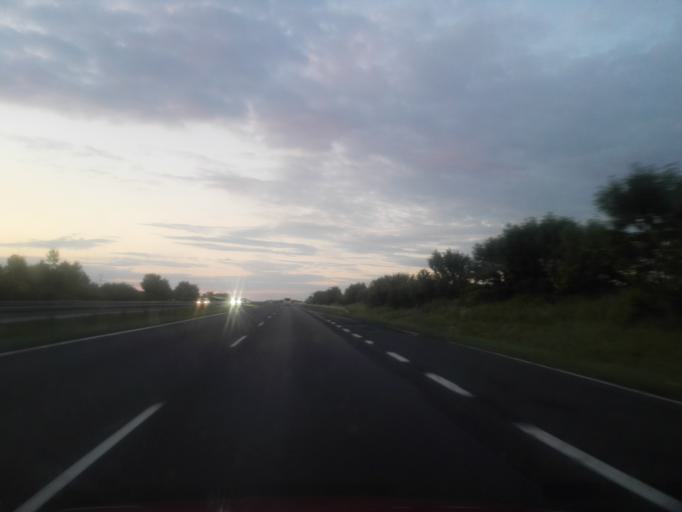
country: PL
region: Lodz Voivodeship
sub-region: Powiat radomszczanski
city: Gomunice
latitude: 51.1823
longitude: 19.4699
